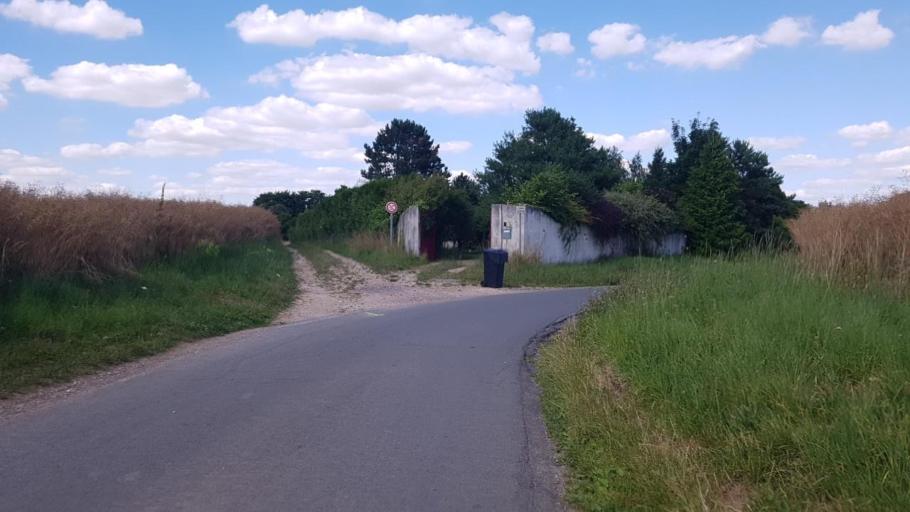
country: FR
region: Picardie
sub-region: Departement de l'Oise
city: Ver-sur-Launette
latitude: 49.1043
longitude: 2.6790
